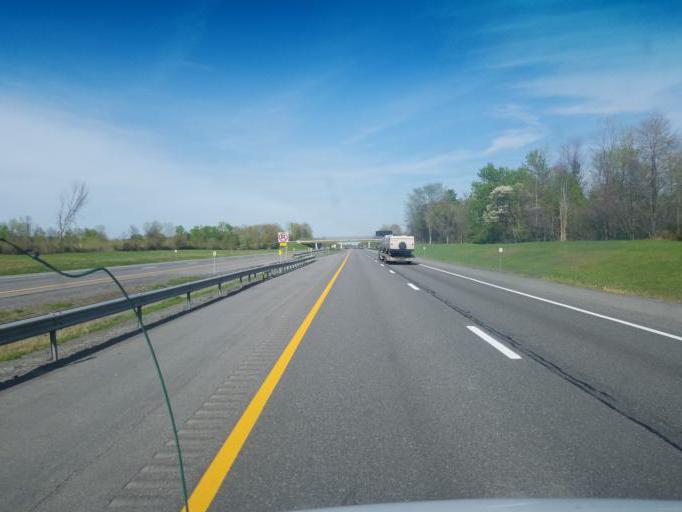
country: US
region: New York
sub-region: Madison County
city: Oneida
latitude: 43.1182
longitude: -75.6380
